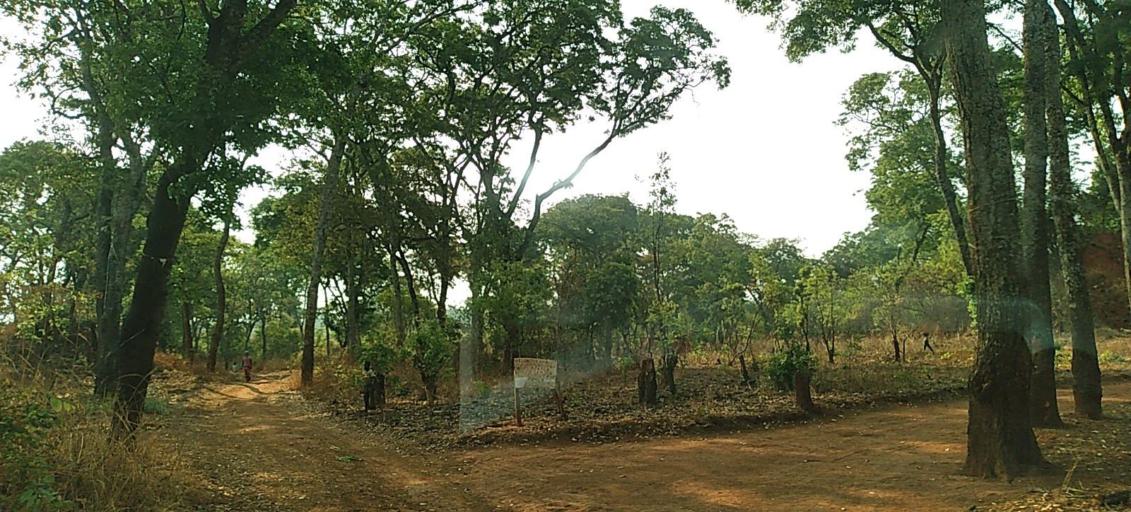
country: ZM
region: North-Western
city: Solwezi
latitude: -12.0552
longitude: 26.1552
